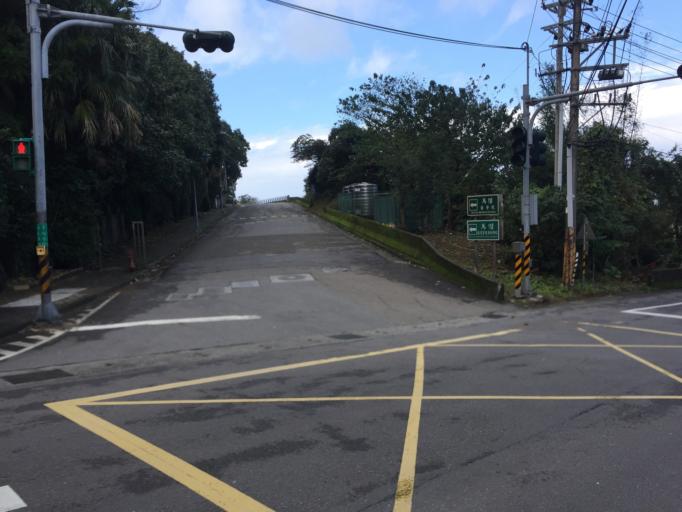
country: TW
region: Taipei
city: Taipei
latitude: 25.2504
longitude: 121.5009
